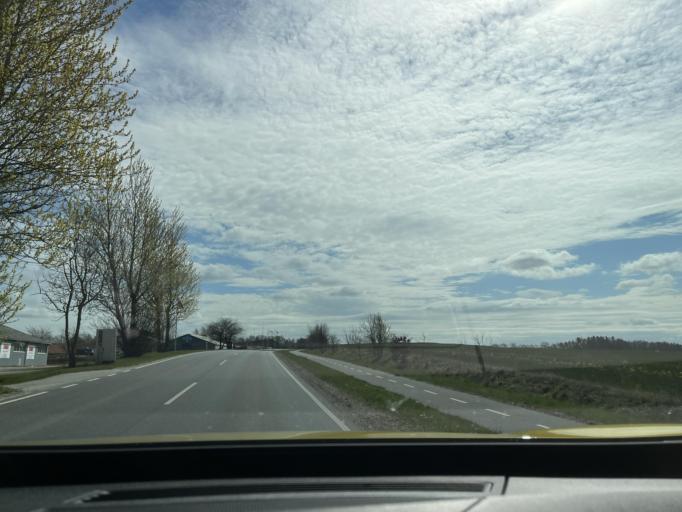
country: DK
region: Central Jutland
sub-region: Favrskov Kommune
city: Hadsten
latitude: 56.3207
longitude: 10.0755
